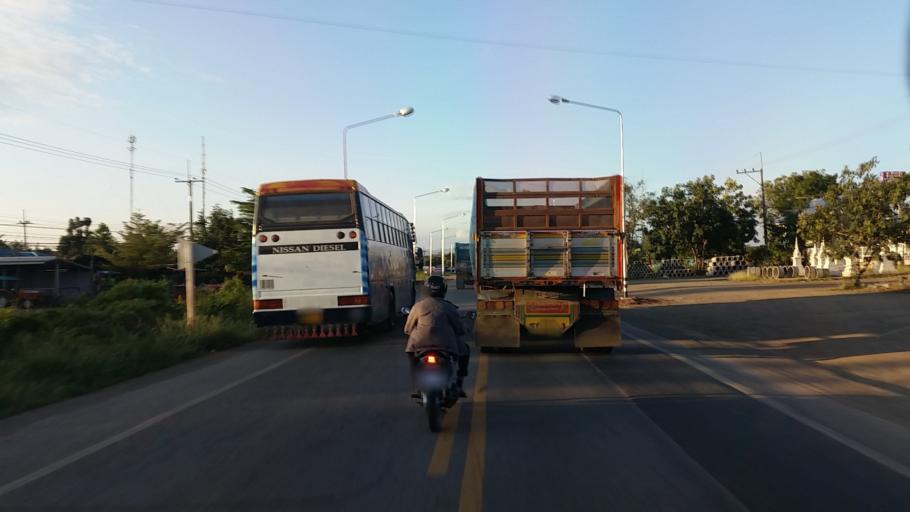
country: TH
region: Lop Buri
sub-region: Amphoe Lam Sonthi
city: Lam Sonthi
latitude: 15.2837
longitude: 101.3485
